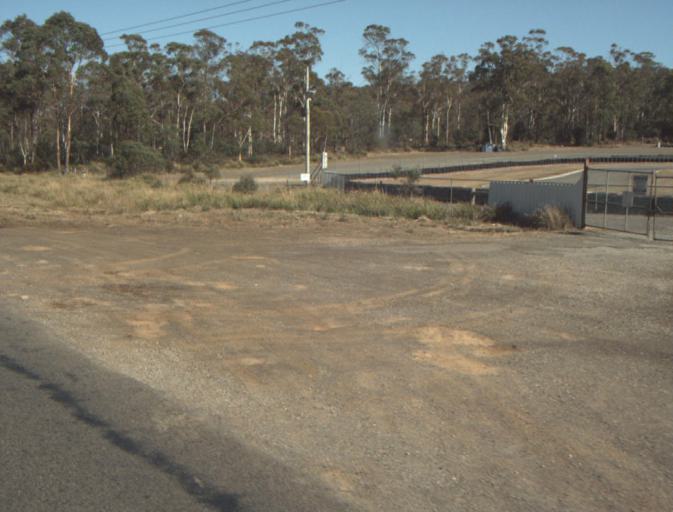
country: AU
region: Tasmania
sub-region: Launceston
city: Mayfield
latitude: -41.3233
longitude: 147.1369
